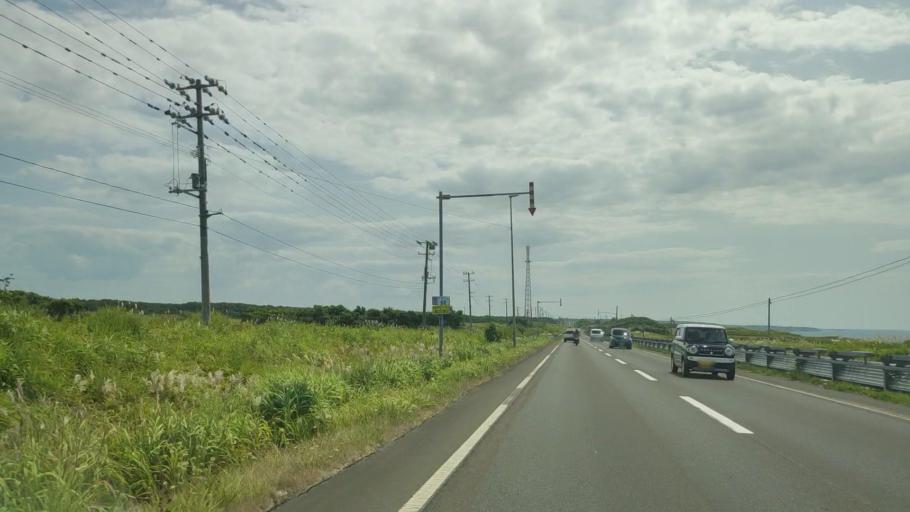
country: JP
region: Hokkaido
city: Rumoi
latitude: 44.4397
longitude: 141.7528
